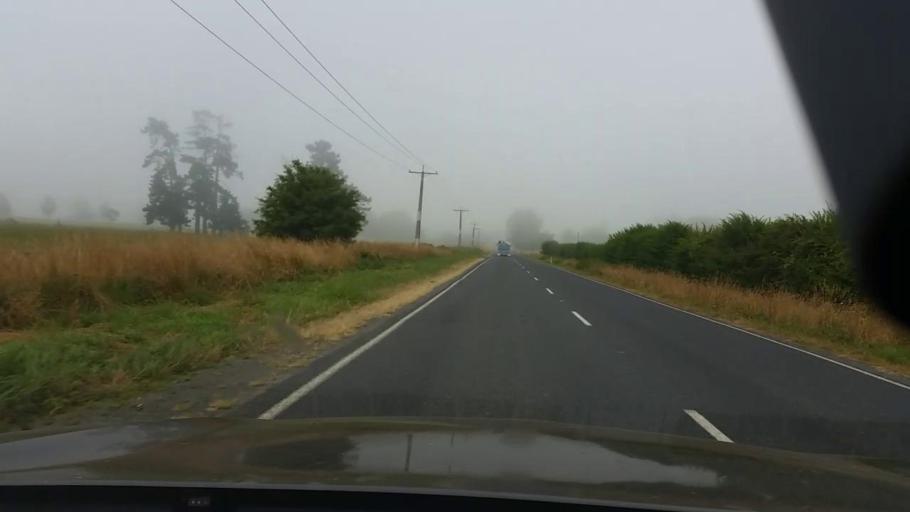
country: NZ
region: Waikato
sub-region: Hamilton City
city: Hamilton
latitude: -37.6354
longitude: 175.3023
